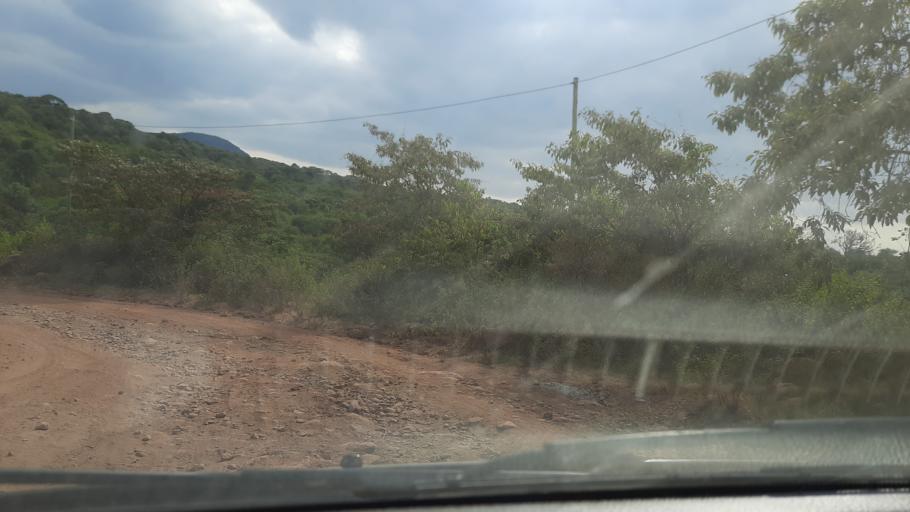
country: TZ
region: Kilimanjaro
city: Moshi
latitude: -2.8591
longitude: 37.2626
